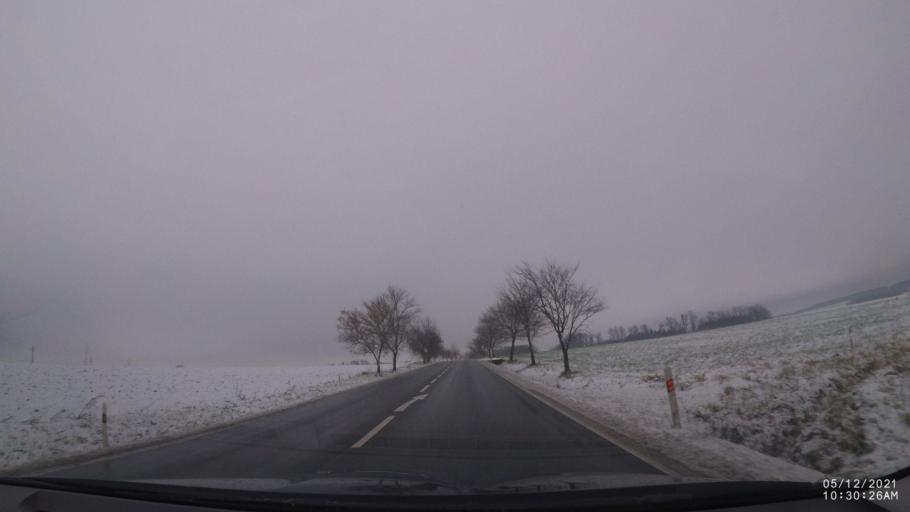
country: CZ
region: Kralovehradecky
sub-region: Okres Rychnov nad Kneznou
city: Rychnov nad Kneznou
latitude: 50.1415
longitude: 16.2846
